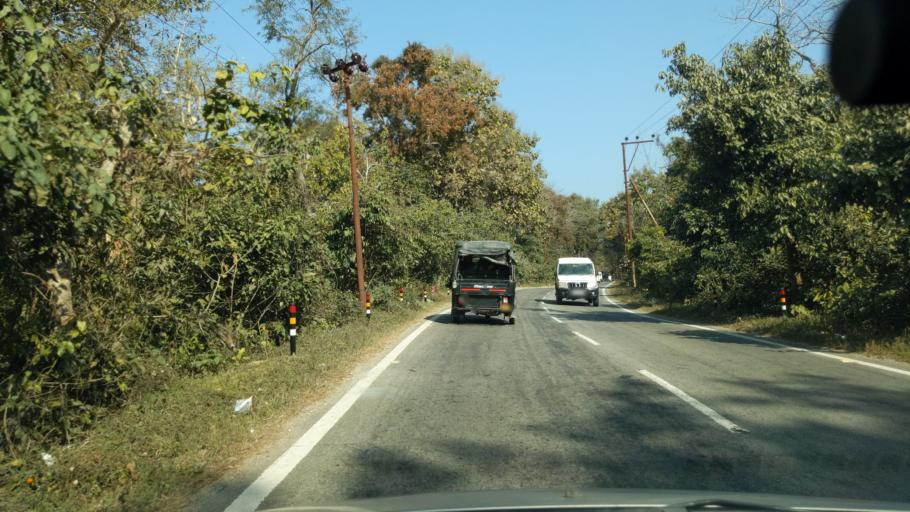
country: IN
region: Uttarakhand
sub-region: Naini Tal
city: Ramnagar
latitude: 29.3791
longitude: 79.1429
